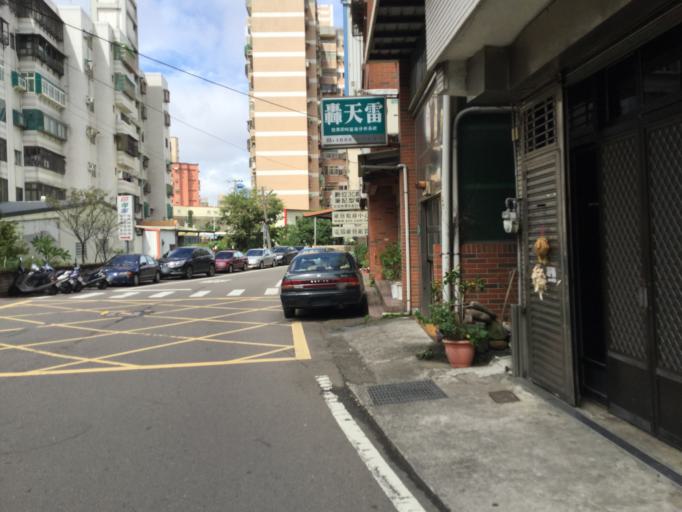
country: TW
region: Taiwan
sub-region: Hsinchu
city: Hsinchu
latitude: 24.7824
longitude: 121.0136
